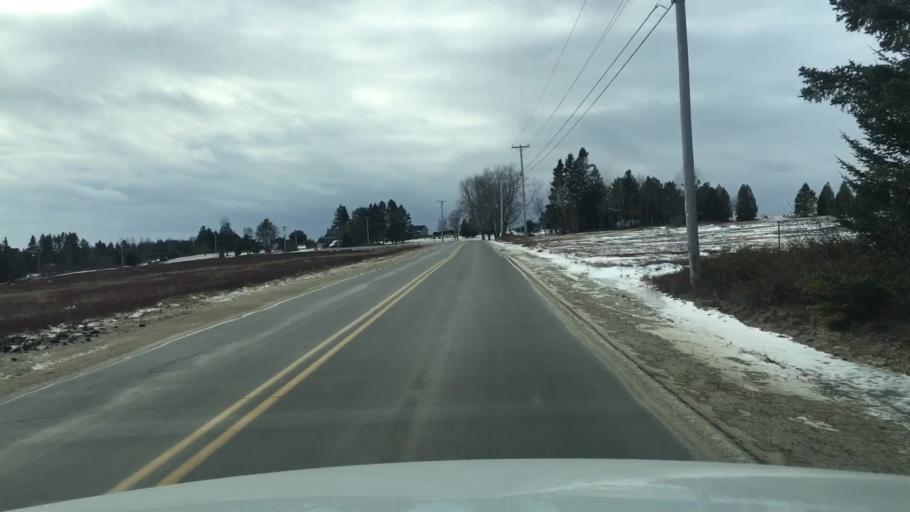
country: US
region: Maine
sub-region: Washington County
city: Jonesport
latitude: 44.6210
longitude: -67.6036
